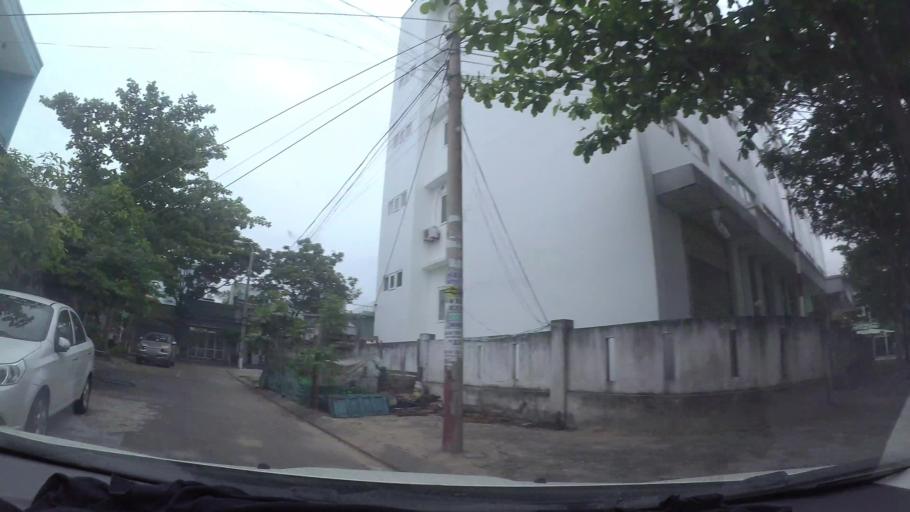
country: VN
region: Da Nang
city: Lien Chieu
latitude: 16.0794
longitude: 108.1589
